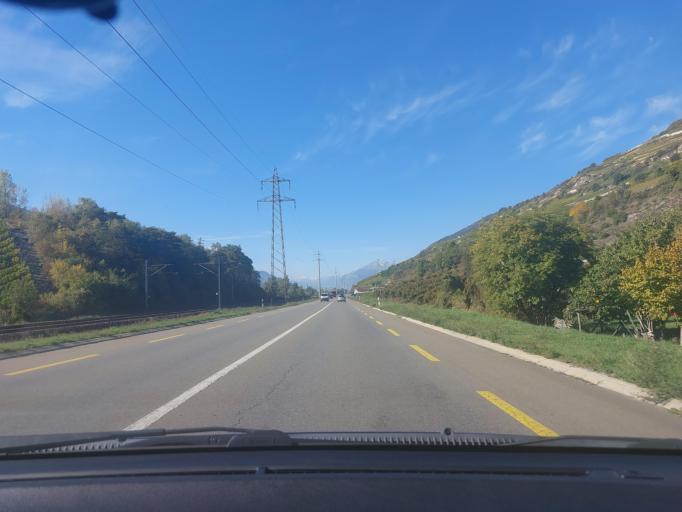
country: CH
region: Valais
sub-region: Sierre District
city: Chalais
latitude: 46.2775
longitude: 7.5016
